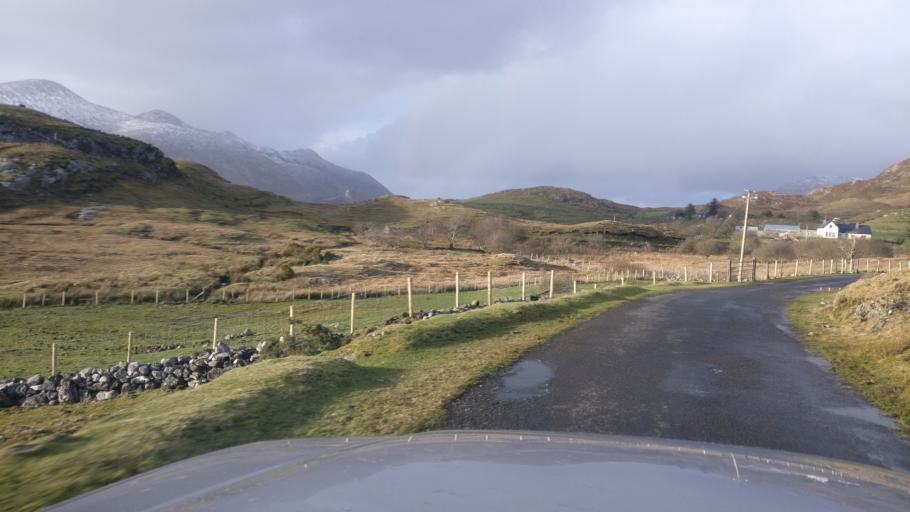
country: IE
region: Connaught
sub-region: County Galway
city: Clifden
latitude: 53.4731
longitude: -9.7287
